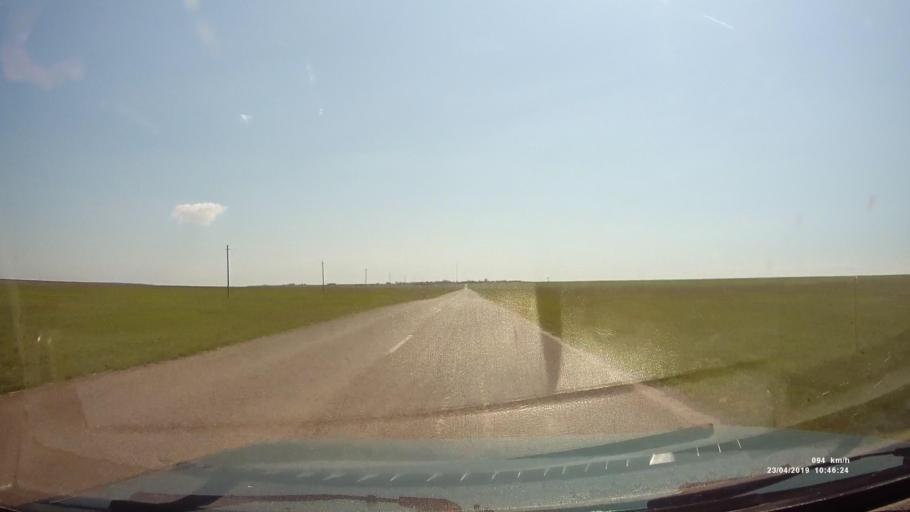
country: RU
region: Kalmykiya
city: Yashalta
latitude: 46.4433
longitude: 42.6906
